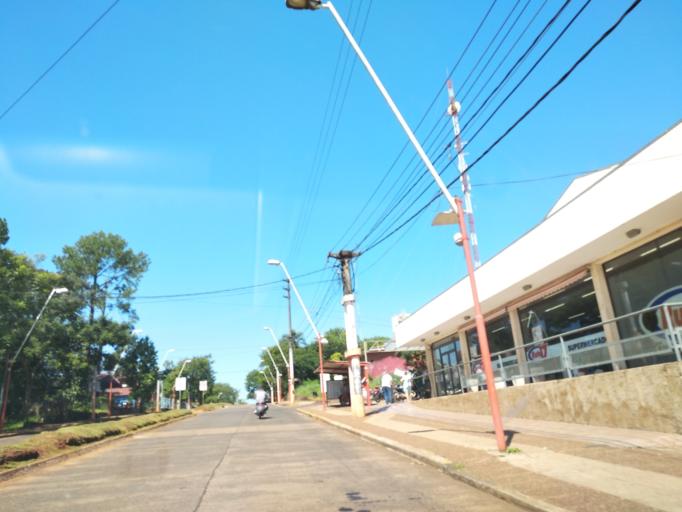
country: AR
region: Misiones
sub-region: Departamento de Iguazu
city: Puerto Iguazu
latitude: -25.6021
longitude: -54.5723
